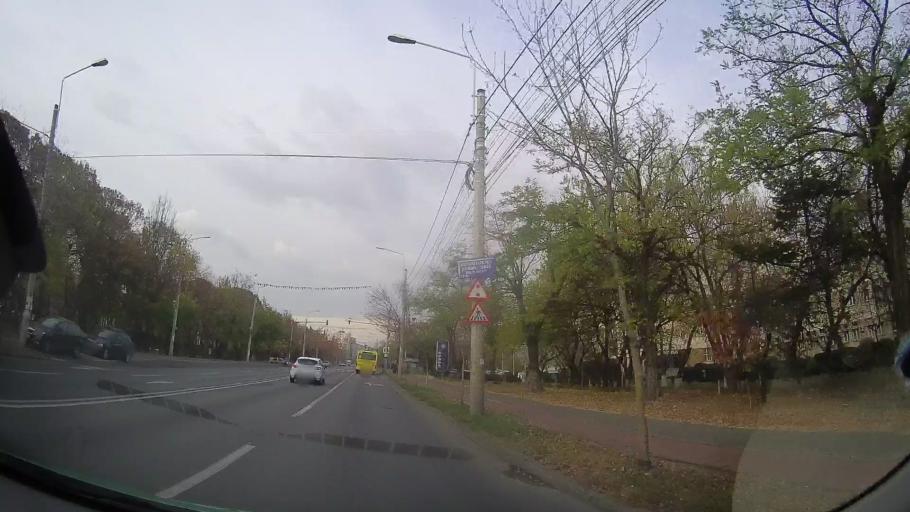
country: RO
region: Prahova
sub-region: Comuna Barcanesti
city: Tatarani
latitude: 44.9136
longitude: 26.0364
